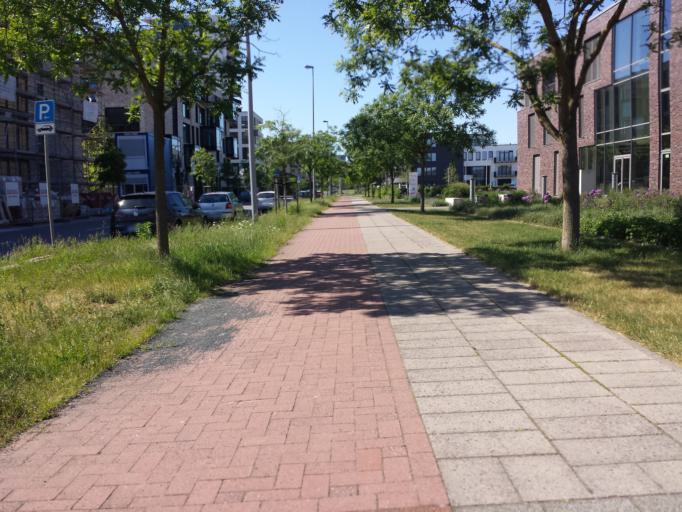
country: DE
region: Bremen
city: Bremen
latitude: 53.0965
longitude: 8.7636
